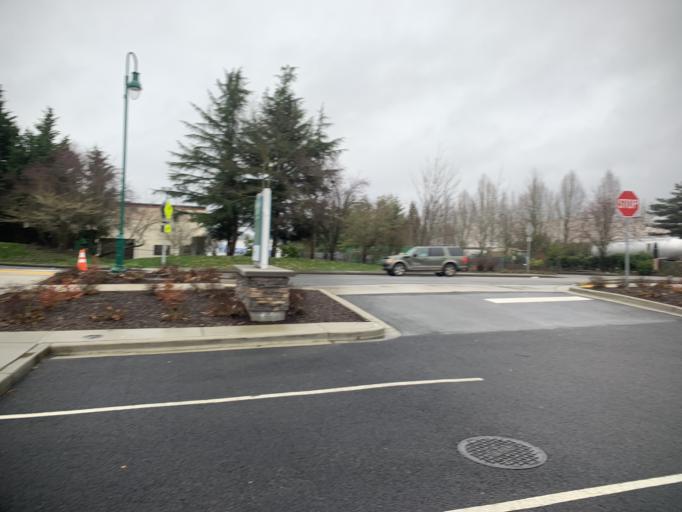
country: US
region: Washington
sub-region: Pierce County
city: Fife
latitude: 47.2278
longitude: -122.3423
